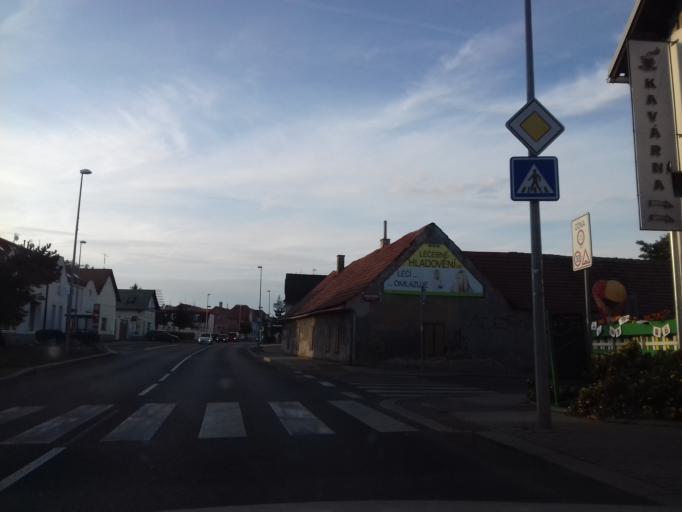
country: CZ
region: Central Bohemia
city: Dolni Brezany
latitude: 50.0099
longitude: 14.4610
